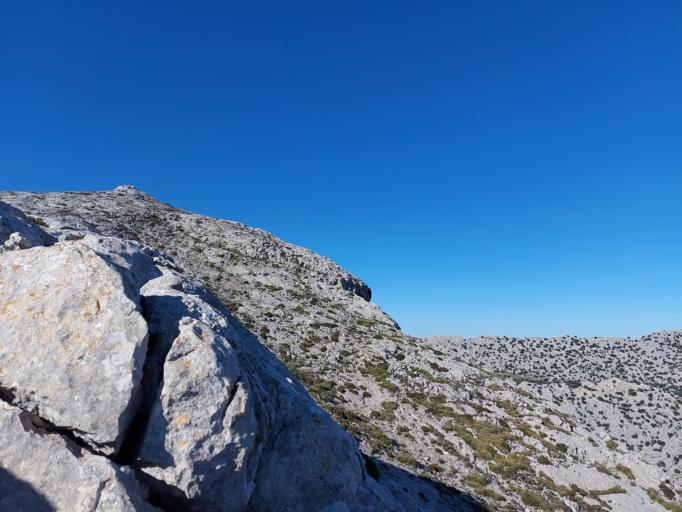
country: ES
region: Balearic Islands
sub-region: Illes Balears
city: Fornalutx
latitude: 39.7746
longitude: 2.7875
